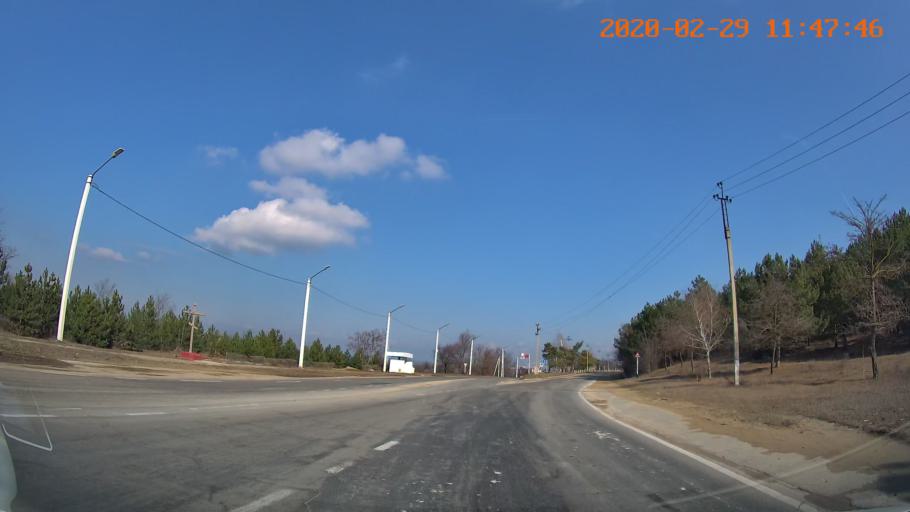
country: MD
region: Rezina
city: Rezina
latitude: 47.7434
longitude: 28.9872
